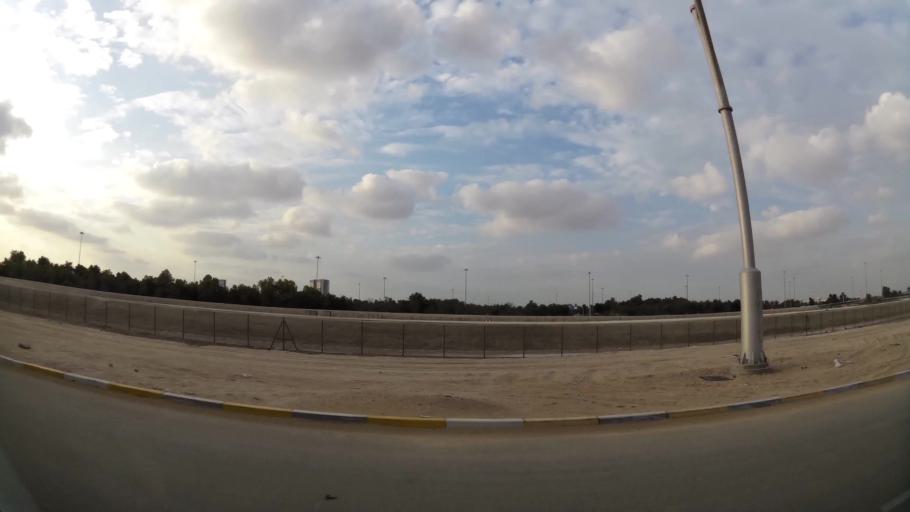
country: AE
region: Abu Dhabi
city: Abu Dhabi
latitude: 24.3876
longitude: 54.5269
